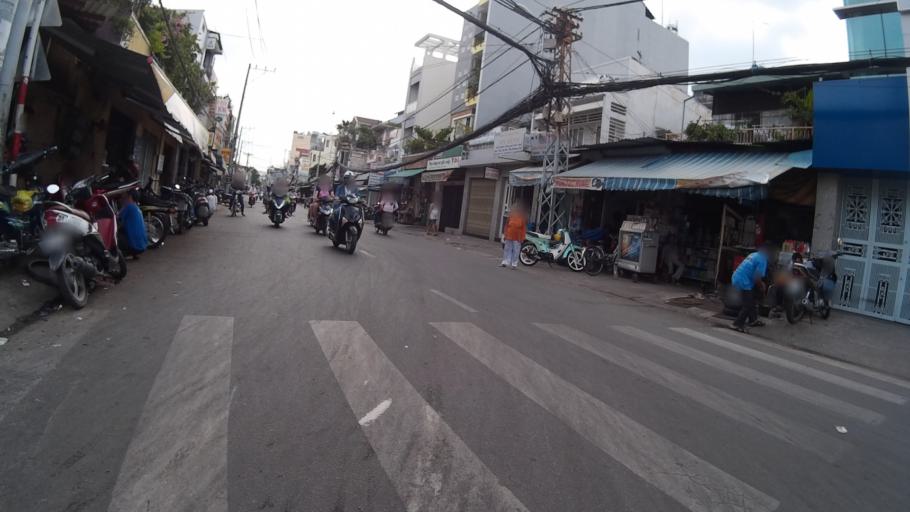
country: VN
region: Ho Chi Minh City
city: Quan Binh Thanh
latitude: 10.7991
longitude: 106.6996
